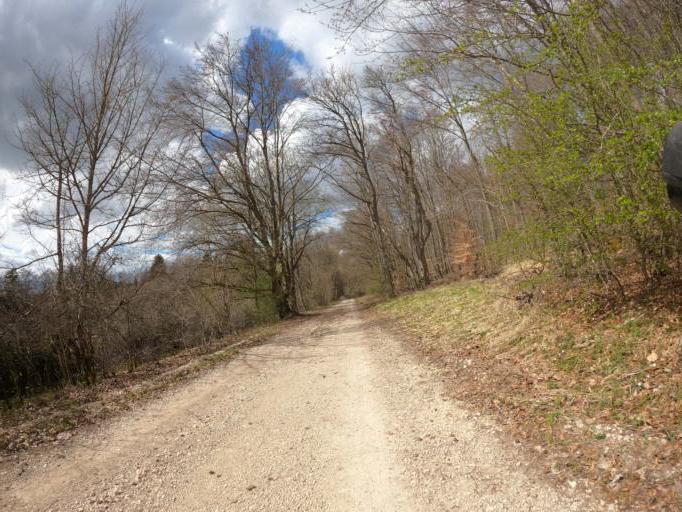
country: DE
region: Baden-Wuerttemberg
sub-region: Tuebingen Region
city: Trochtelfingen
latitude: 48.3844
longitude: 9.2231
